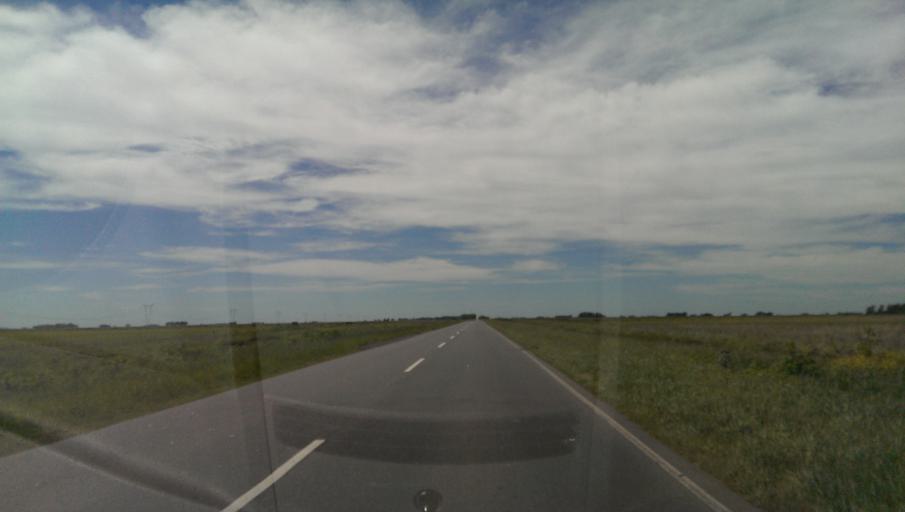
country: AR
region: Buenos Aires
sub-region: Partido de Laprida
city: Laprida
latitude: -37.2272
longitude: -60.7043
